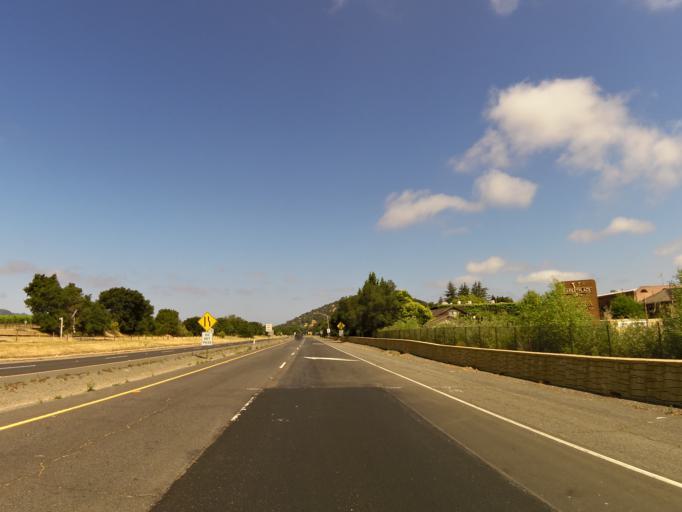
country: US
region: California
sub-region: Napa County
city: Yountville
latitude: 38.4002
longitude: -122.3620
